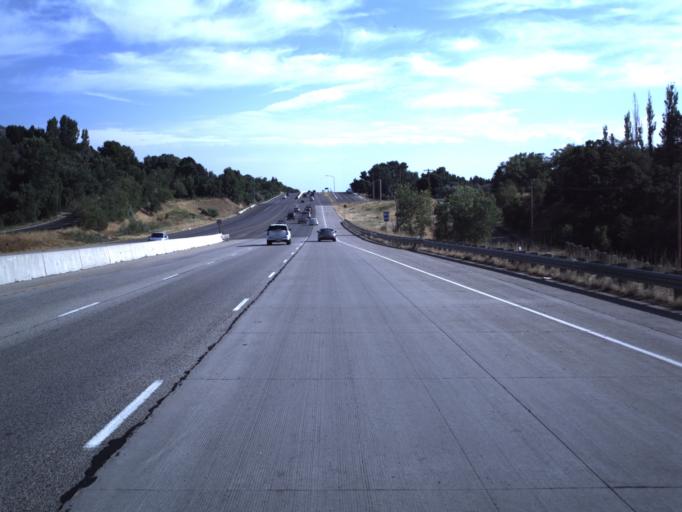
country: US
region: Utah
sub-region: Davis County
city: South Weber
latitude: 41.1037
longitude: -111.9103
